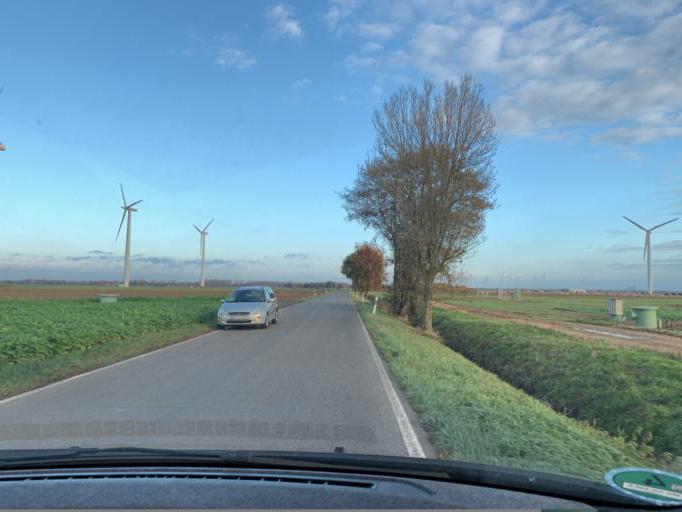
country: DE
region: North Rhine-Westphalia
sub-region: Regierungsbezirk Koln
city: Titz
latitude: 51.0608
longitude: 6.4071
